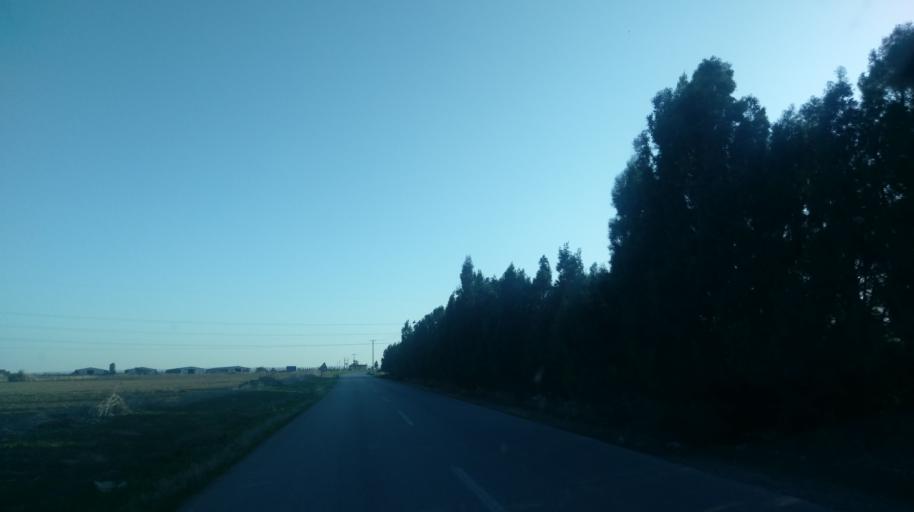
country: CY
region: Ammochostos
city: Lefkonoiko
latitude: 35.2097
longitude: 33.6196
